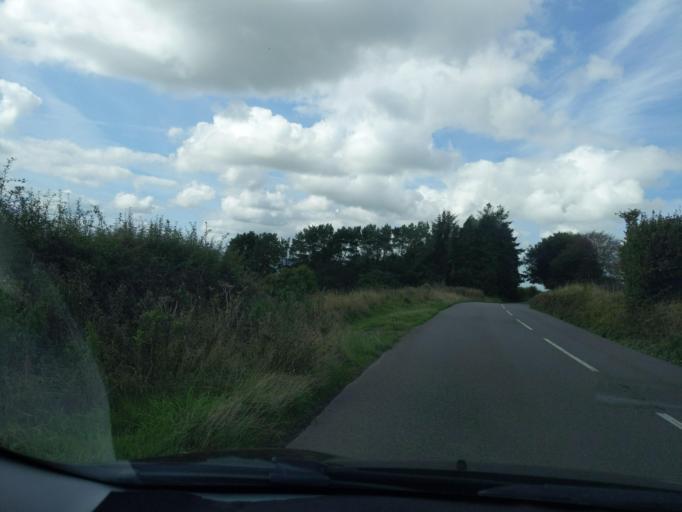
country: GB
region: England
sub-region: Cornwall
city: Callington
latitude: 50.5114
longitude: -4.3071
